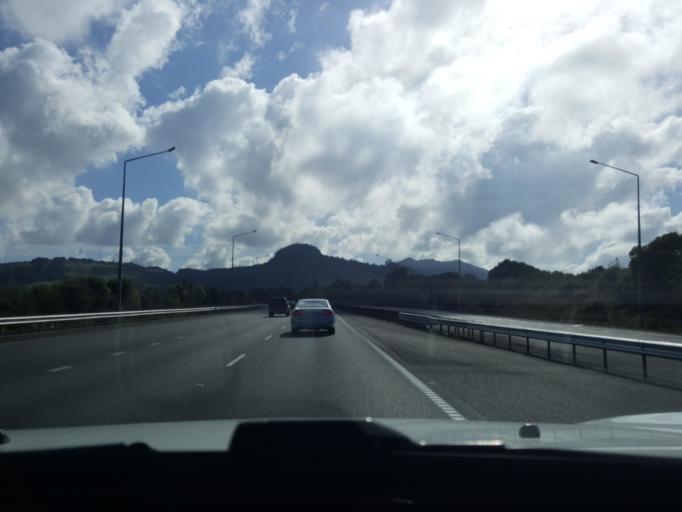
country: NZ
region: Auckland
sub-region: Auckland
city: Pukekohe East
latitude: -37.2369
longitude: 175.0203
